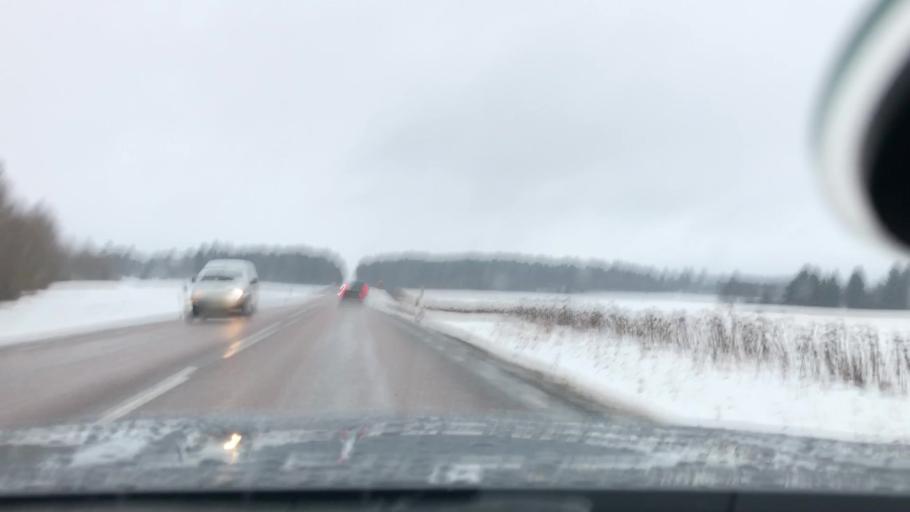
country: SE
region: Stockholm
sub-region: Sodertalje Kommun
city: Pershagen
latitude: 59.0490
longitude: 17.6074
